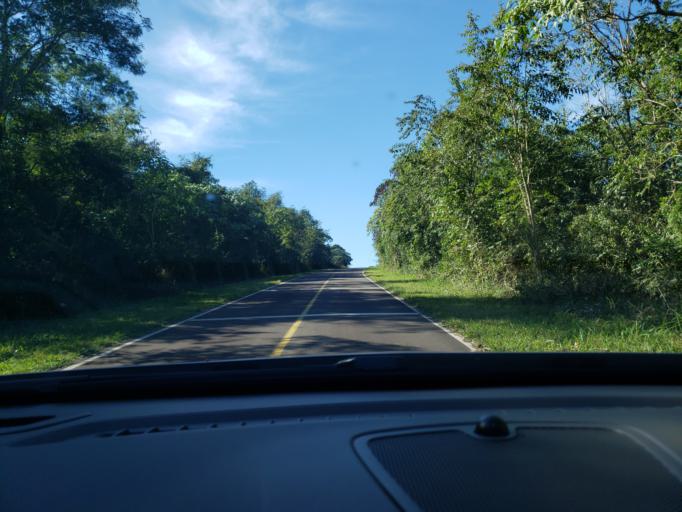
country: BR
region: Rio Grande do Sul
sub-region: Tres Passos
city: Tres Passos
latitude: -27.1516
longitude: -53.9105
